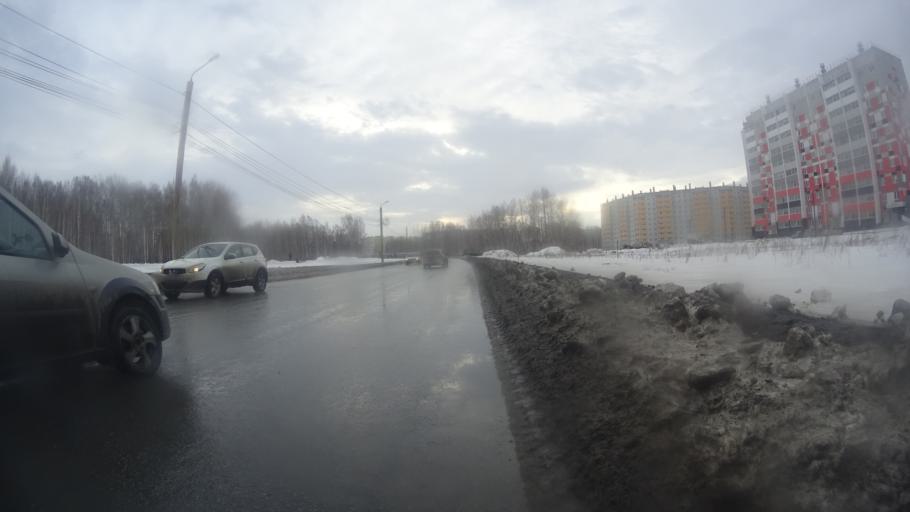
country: RU
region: Chelyabinsk
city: Roshchino
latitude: 55.2168
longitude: 61.2886
